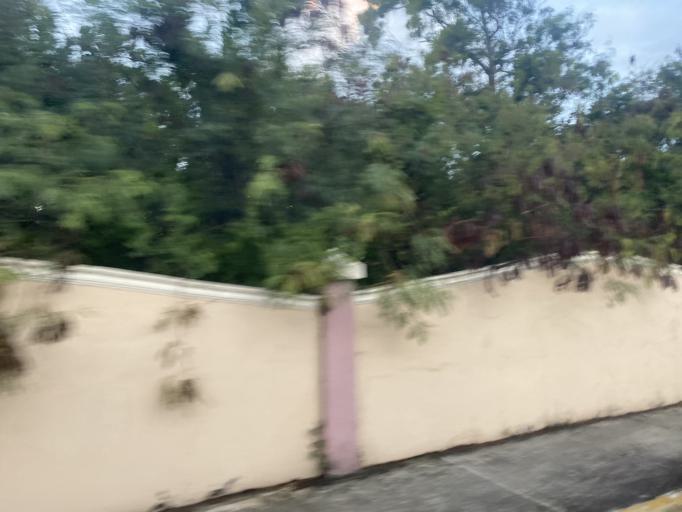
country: DO
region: San Juan
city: Punta Cana
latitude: 18.7118
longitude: -68.4603
